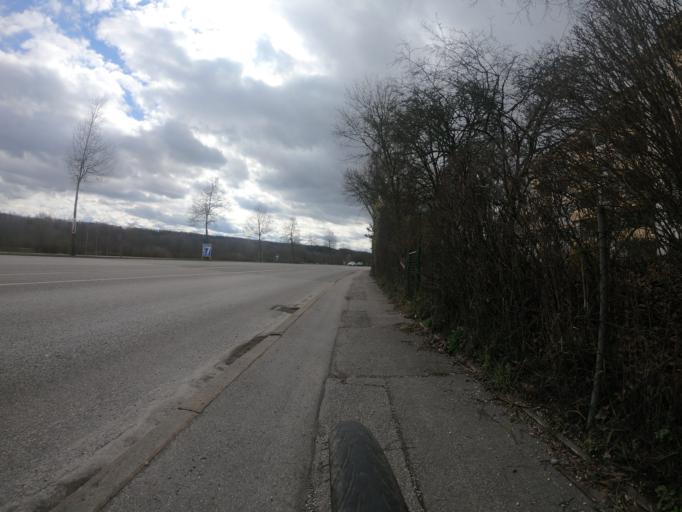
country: DE
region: Bavaria
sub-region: Upper Bavaria
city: Fuerstenfeldbruck
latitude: 48.1700
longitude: 11.2393
